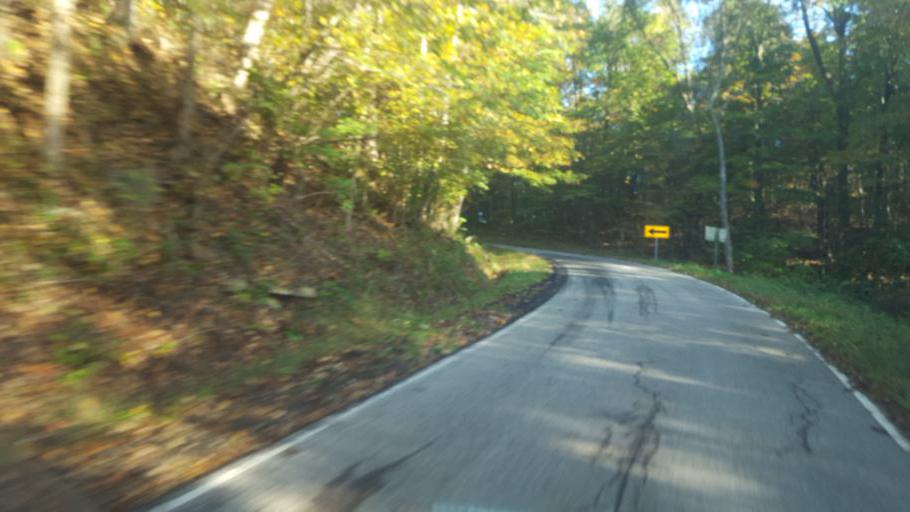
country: US
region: Ohio
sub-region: Adams County
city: Manchester
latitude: 38.5193
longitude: -83.5135
